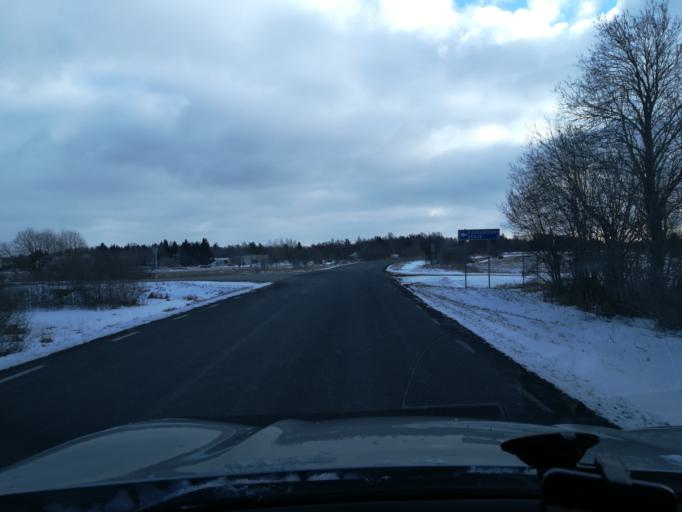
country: EE
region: Harju
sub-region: Harku vald
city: Tabasalu
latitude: 59.4243
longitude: 24.4208
